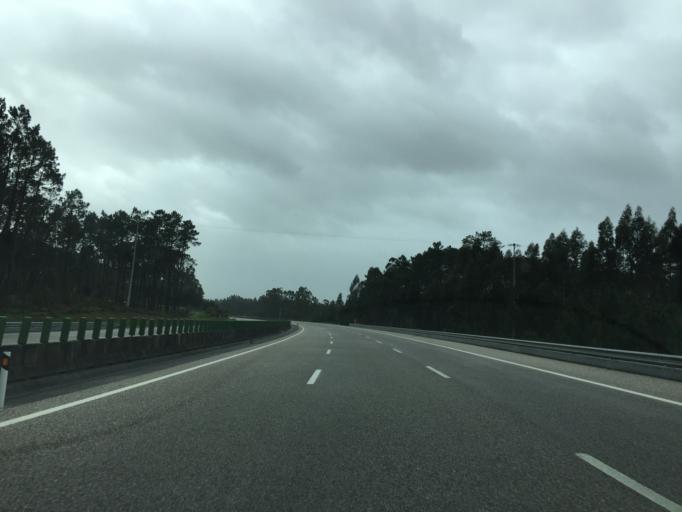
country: PT
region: Leiria
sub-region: Leiria
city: Monte Redondo
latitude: 39.9229
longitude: -8.7909
